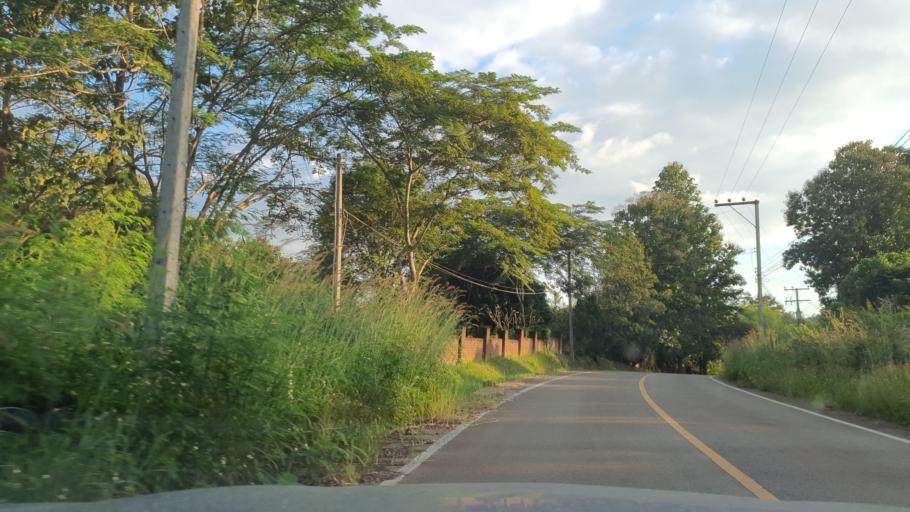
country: TH
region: Chiang Mai
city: Mae On
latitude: 18.8600
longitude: 99.2475
